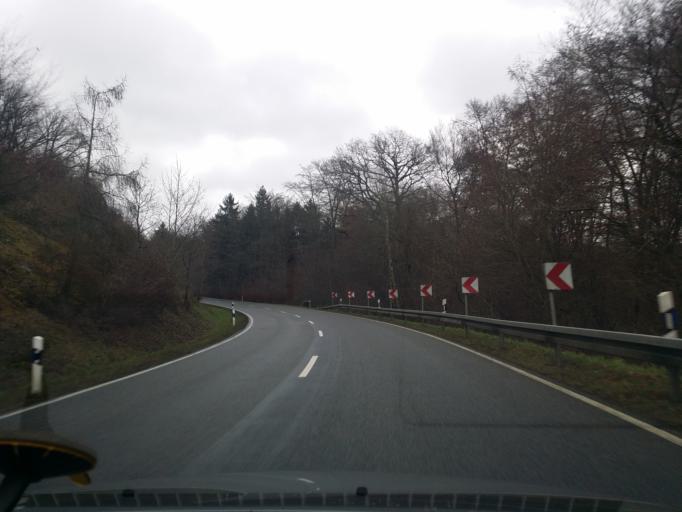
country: DE
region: Hesse
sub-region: Regierungsbezirk Darmstadt
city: Waldems
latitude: 50.2434
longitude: 8.3477
